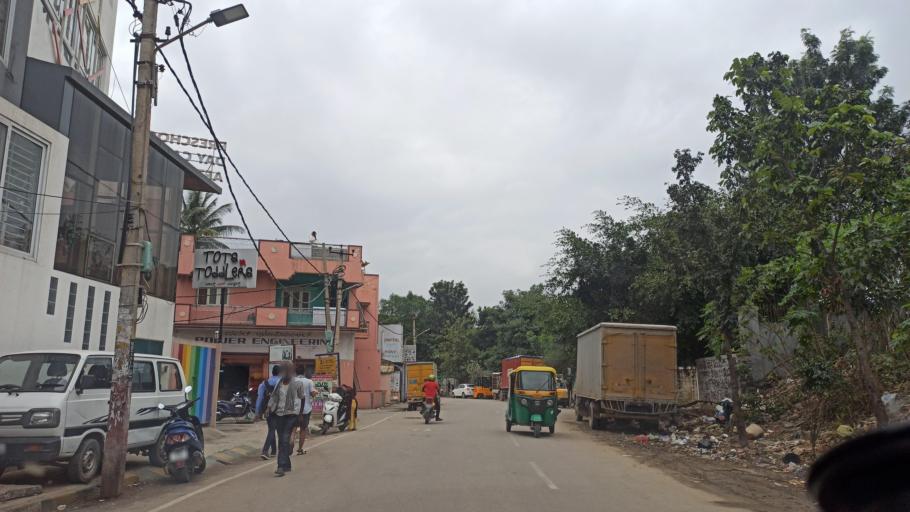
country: IN
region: Karnataka
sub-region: Bangalore Urban
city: Bangalore
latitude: 12.9969
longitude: 77.6779
